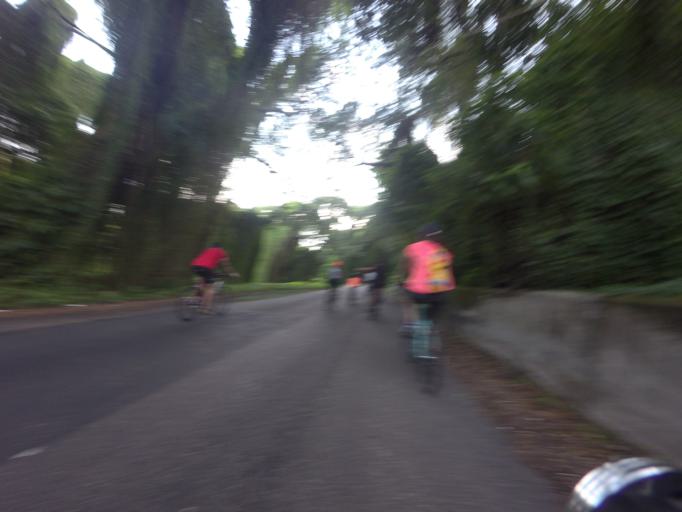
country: CU
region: La Habana
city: Cerro
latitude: 23.1132
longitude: -82.4068
